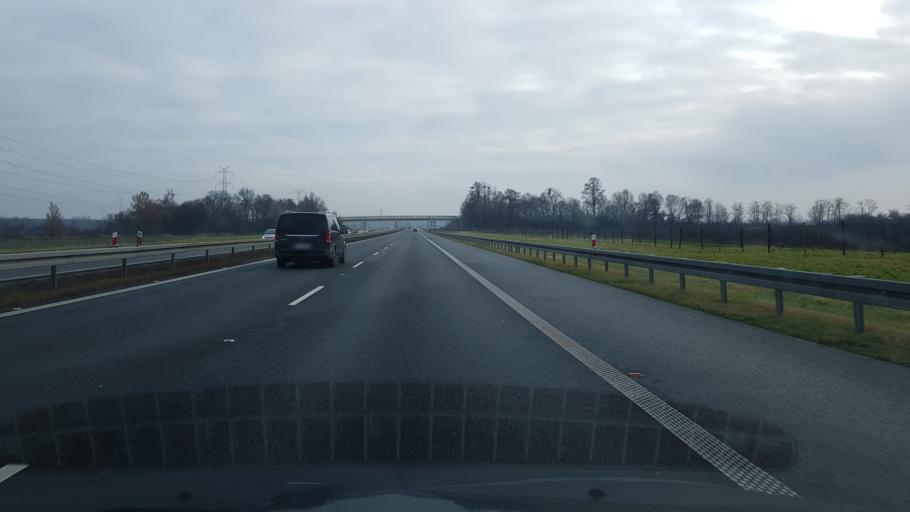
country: PL
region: Lower Silesian Voivodeship
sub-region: Powiat strzelinski
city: Wiazow
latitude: 50.8599
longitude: 17.2239
